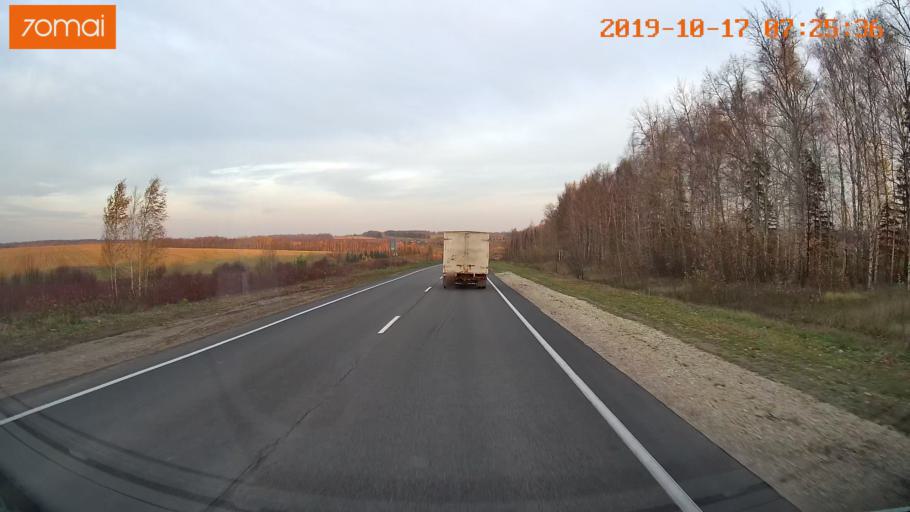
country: RU
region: Ivanovo
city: Gavrilov Posad
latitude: 56.3507
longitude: 40.1016
